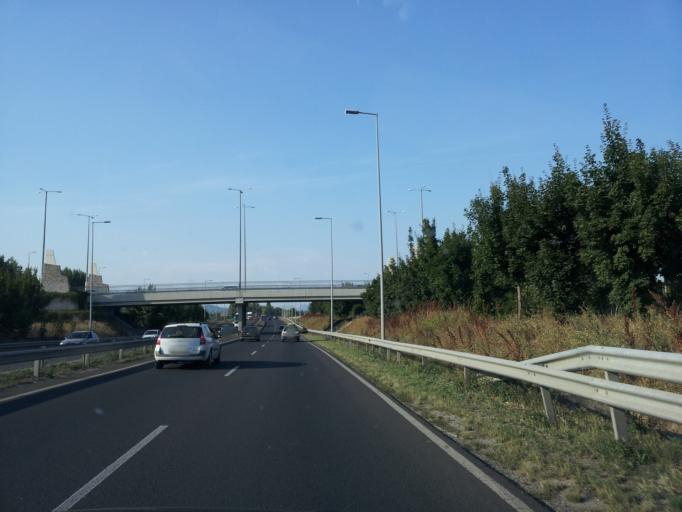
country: HU
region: Pest
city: Budakalasz
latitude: 47.6191
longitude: 19.0664
